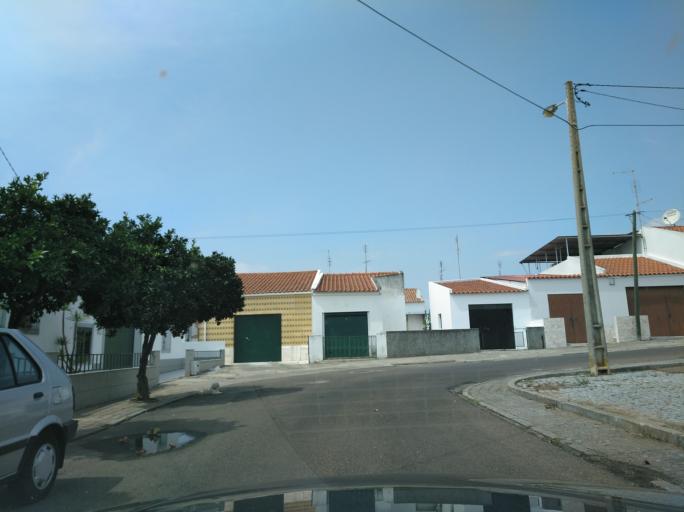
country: PT
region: Portalegre
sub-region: Campo Maior
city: Campo Maior
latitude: 39.0176
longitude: -7.0677
